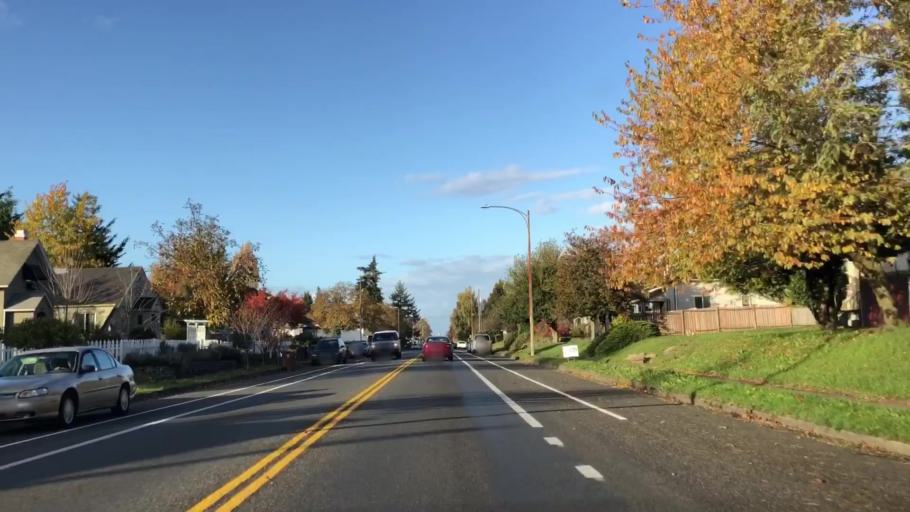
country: US
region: Washington
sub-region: Pierce County
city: Parkland
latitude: 47.2021
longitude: -122.4432
